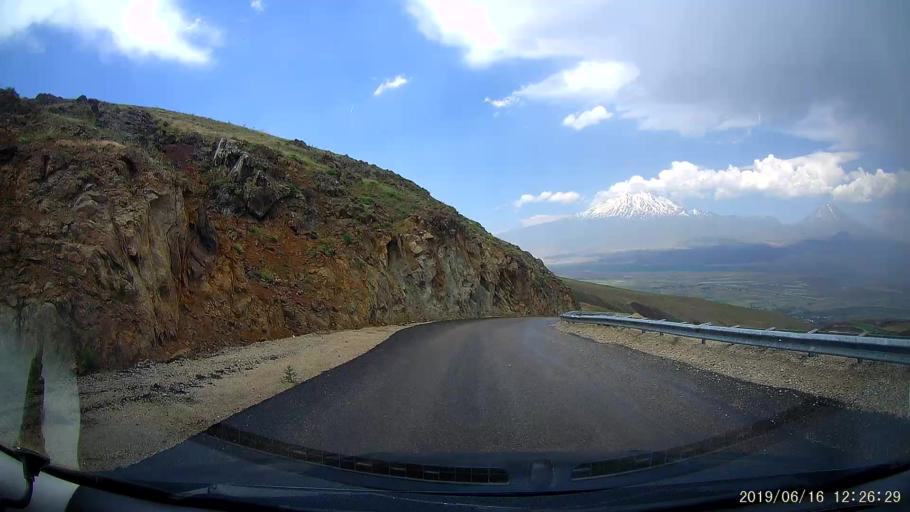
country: TR
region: Agri
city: Dogubayazit
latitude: 39.4452
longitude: 44.2361
